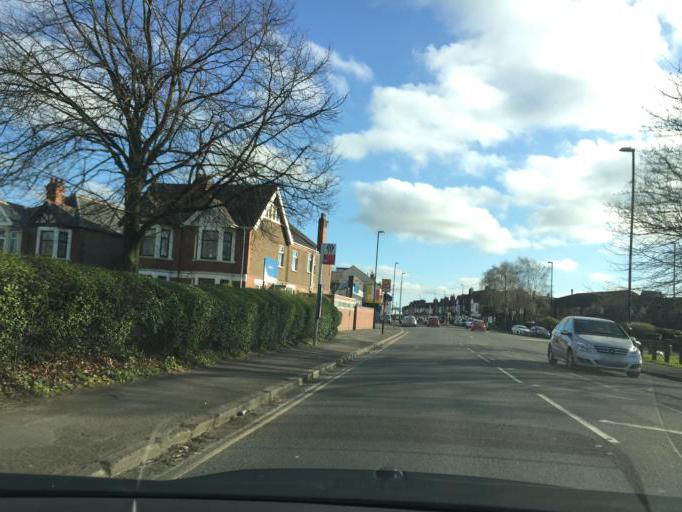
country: GB
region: England
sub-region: Coventry
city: Coventry
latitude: 52.4050
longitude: -1.4866
